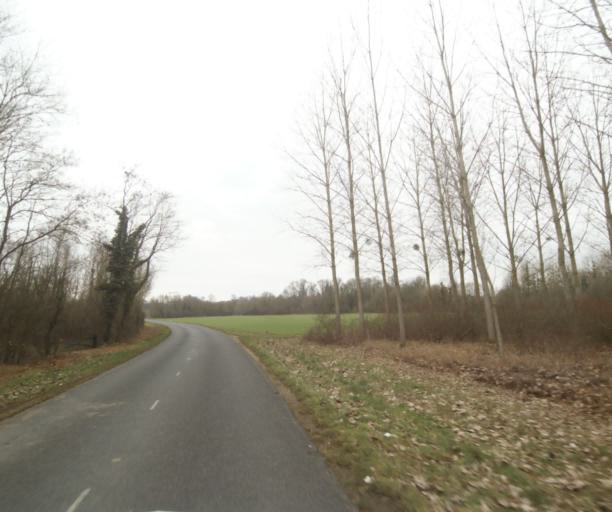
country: FR
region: Champagne-Ardenne
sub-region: Departement de la Haute-Marne
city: Villiers-en-Lieu
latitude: 48.6429
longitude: 4.8392
